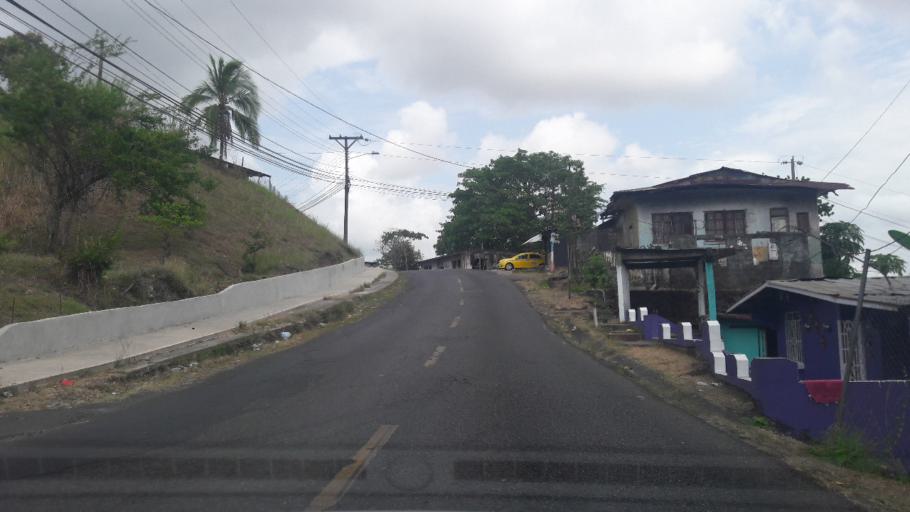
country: PA
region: Panama
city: Alcalde Diaz
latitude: 9.1143
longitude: -79.5555
